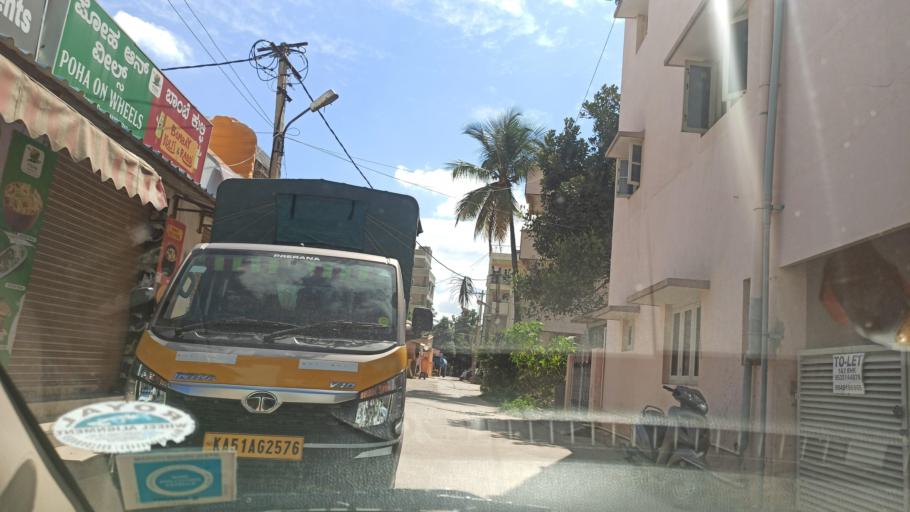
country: IN
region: Karnataka
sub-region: Bangalore Urban
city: Bangalore
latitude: 12.9290
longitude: 77.6777
